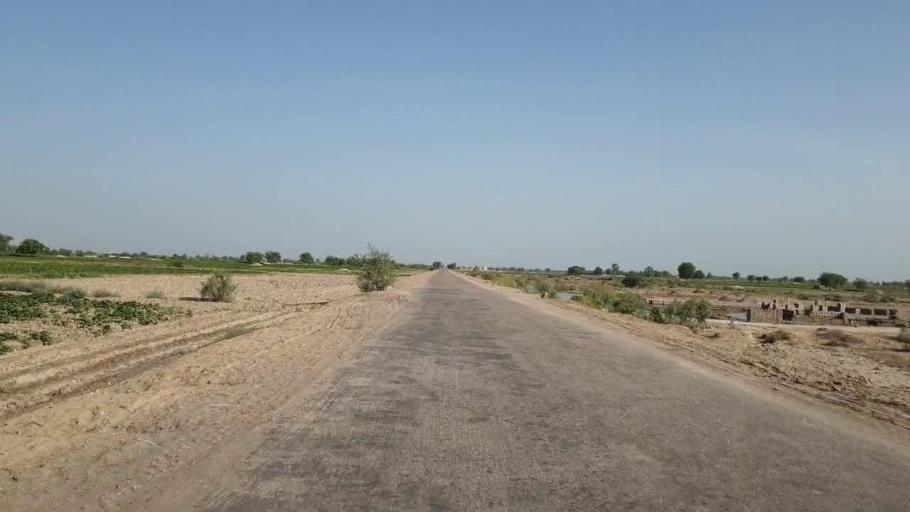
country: PK
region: Sindh
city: Nawabshah
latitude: 26.1477
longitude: 68.4491
